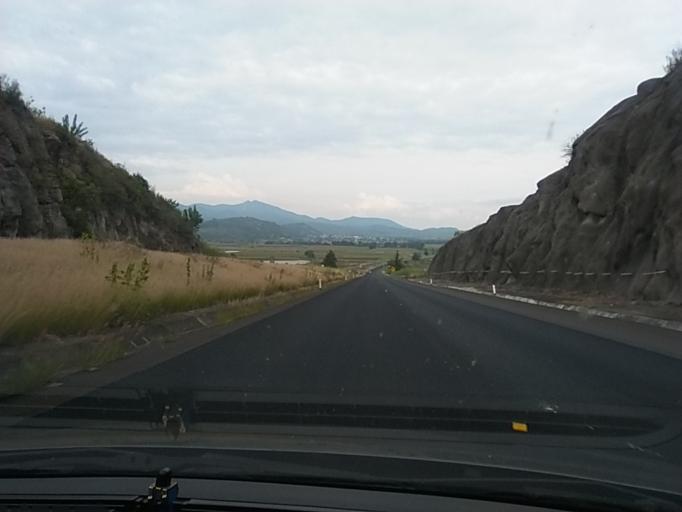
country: MX
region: Mexico
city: Huaniqueo de Morales
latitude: 19.8932
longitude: -101.5499
